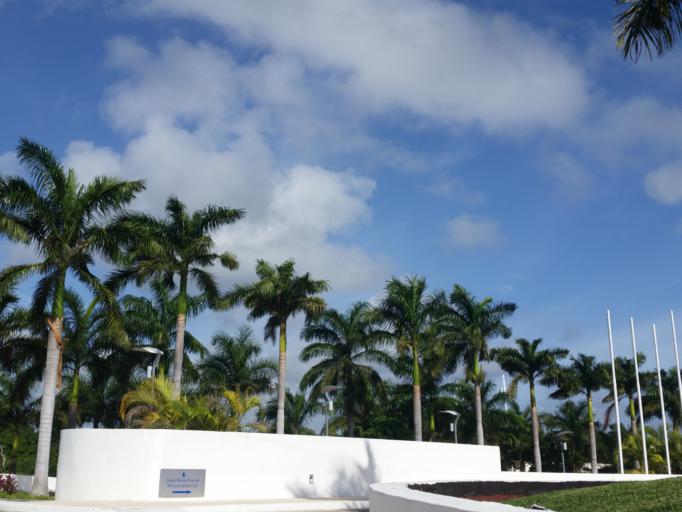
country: MX
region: Quintana Roo
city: Playa del Carmen
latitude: 20.6729
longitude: -87.0344
